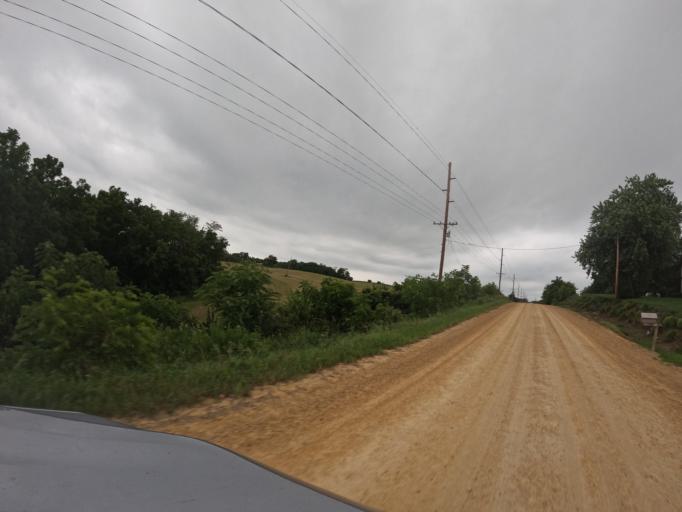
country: US
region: Iowa
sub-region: Jackson County
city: Maquoketa
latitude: 41.9381
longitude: -90.6315
